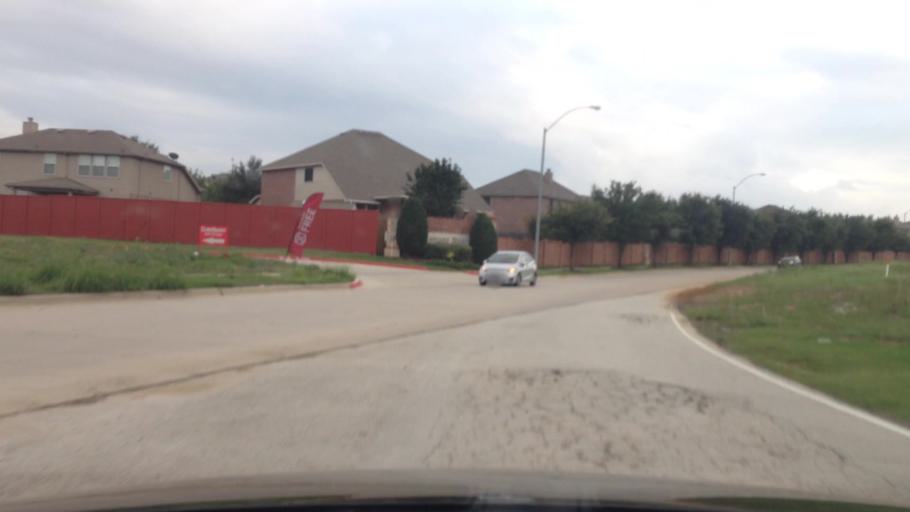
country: US
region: Texas
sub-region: Tarrant County
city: Crowley
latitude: 32.5769
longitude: -97.3288
